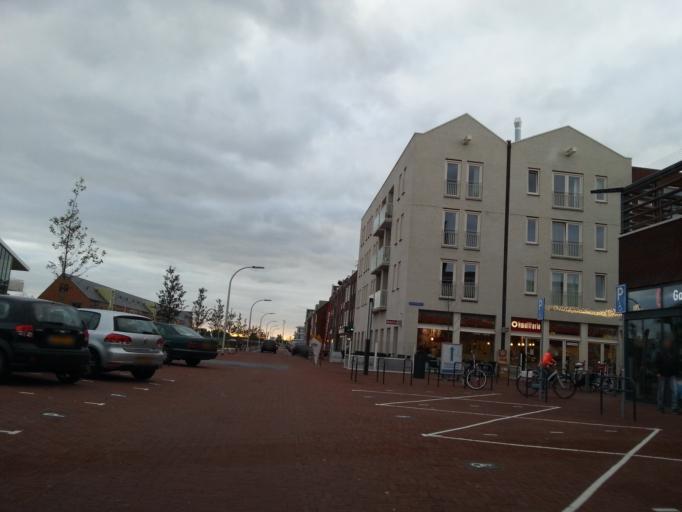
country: NL
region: South Holland
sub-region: Gemeente Pijnacker-Nootdorp
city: Pijnacker
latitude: 52.0039
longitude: 4.4436
